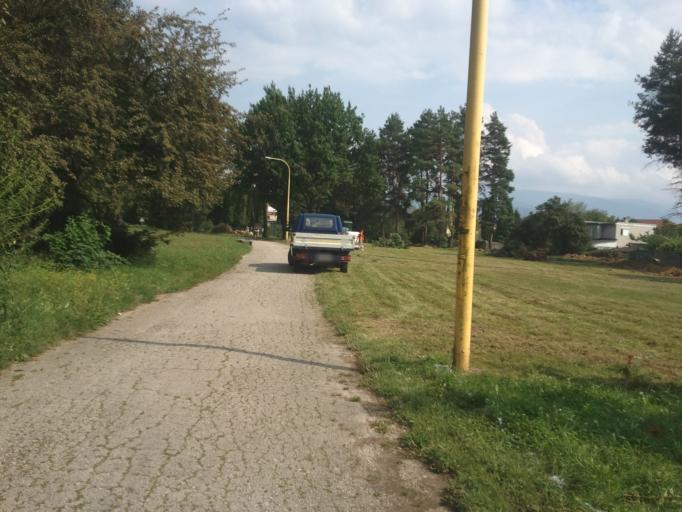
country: SK
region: Nitriansky
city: Bojnice
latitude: 48.7742
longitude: 18.5972
